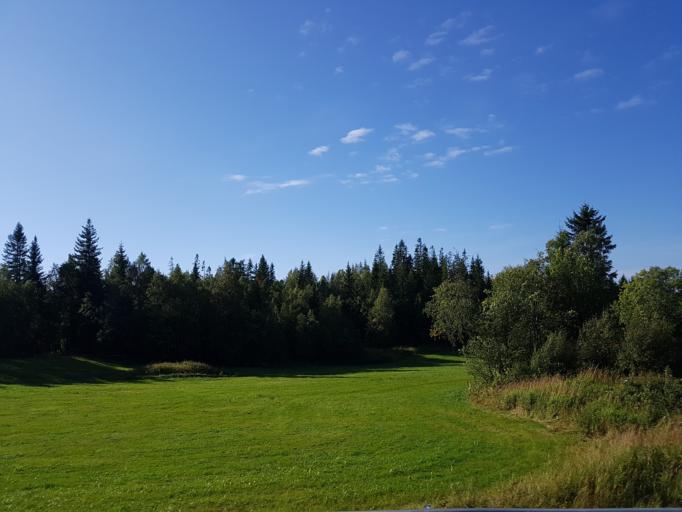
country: NO
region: Sor-Trondelag
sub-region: Trondheim
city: Trondheim
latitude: 63.6519
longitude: 10.2586
